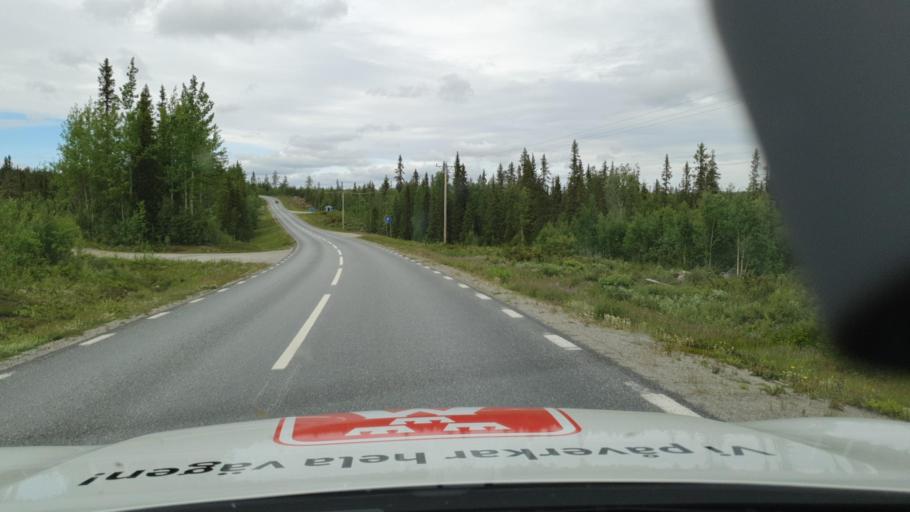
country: SE
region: Vaesterbotten
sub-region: Lycksele Kommun
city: Soderfors
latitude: 64.3870
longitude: 18.0035
